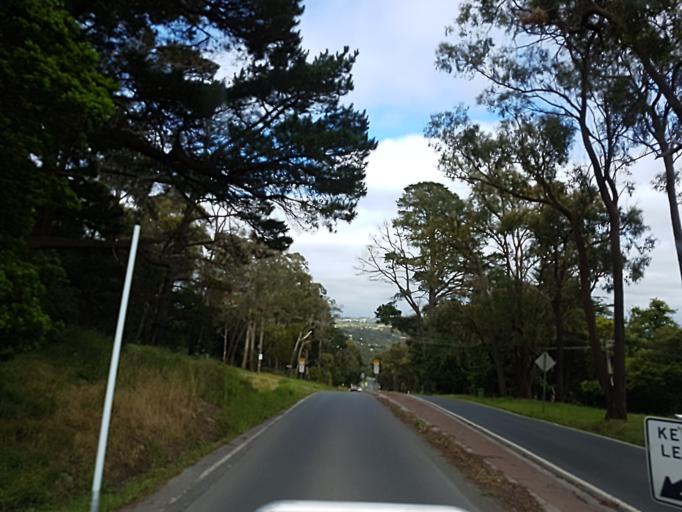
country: AU
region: Victoria
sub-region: Yarra Ranges
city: Mount Evelyn
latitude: -37.7826
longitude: 145.3714
